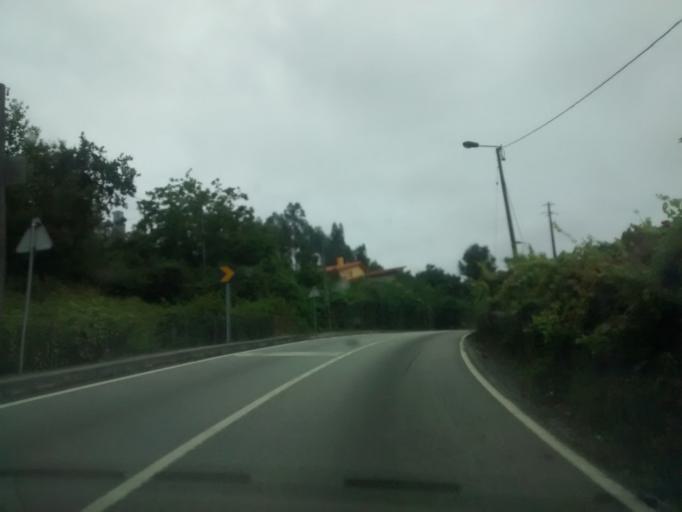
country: PT
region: Braga
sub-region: Braga
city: Oliveira
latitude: 41.4667
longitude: -8.4891
